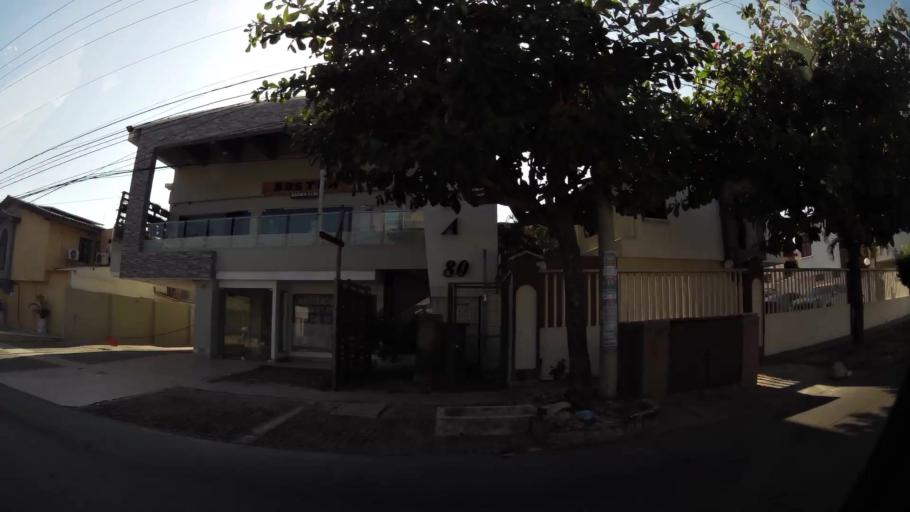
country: CO
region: Atlantico
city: Barranquilla
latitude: 11.0195
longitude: -74.8043
